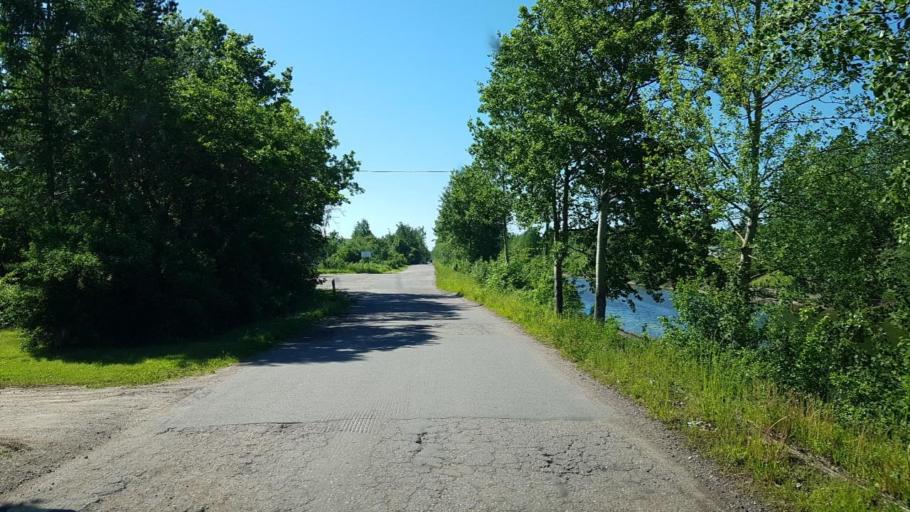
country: EE
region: Ida-Virumaa
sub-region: Narva linn
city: Narva
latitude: 59.3503
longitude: 28.1638
